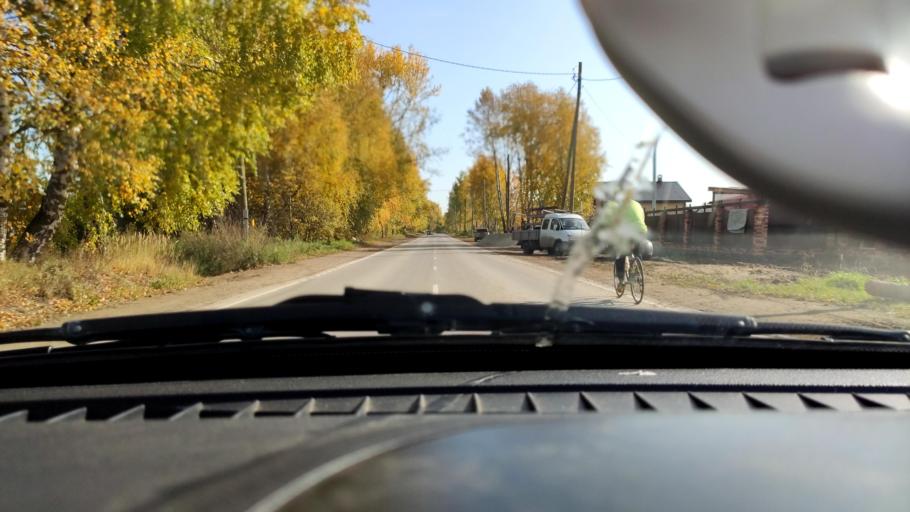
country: RU
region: Perm
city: Overyata
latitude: 58.0560
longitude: 55.8716
